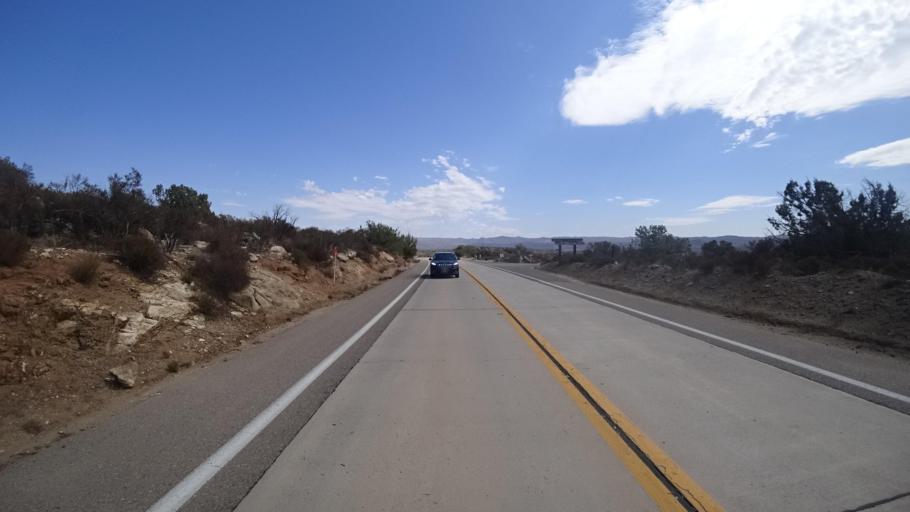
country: MX
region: Baja California
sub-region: Tecate
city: Cereso del Hongo
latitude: 32.6187
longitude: -116.2155
